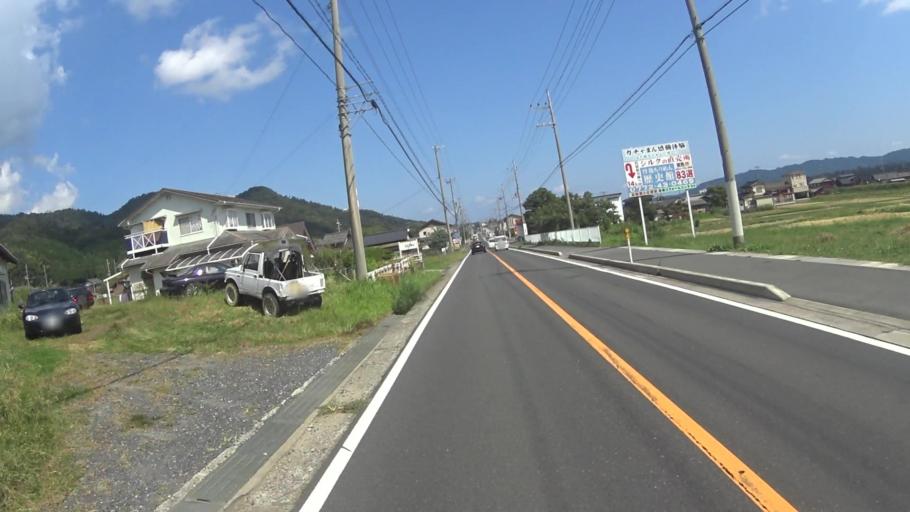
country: JP
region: Kyoto
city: Miyazu
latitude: 35.5770
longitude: 135.1811
